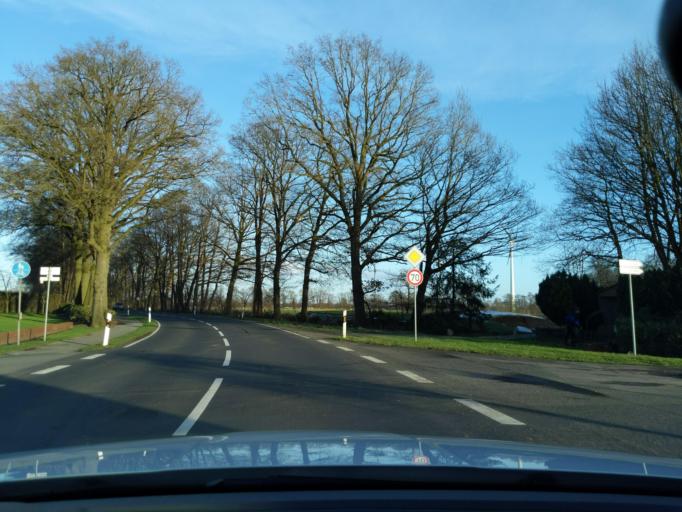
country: DE
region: Lower Saxony
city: Meppen
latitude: 52.6585
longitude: 7.3518
